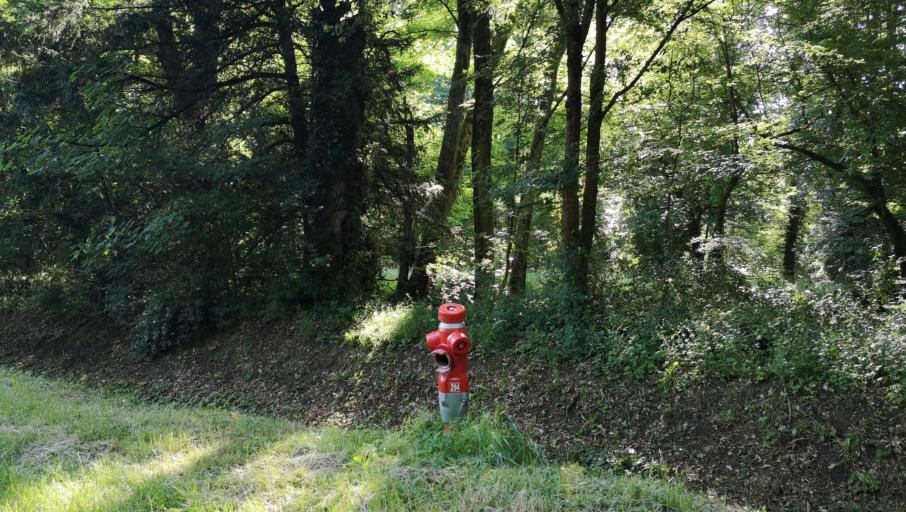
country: FR
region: Centre
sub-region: Departement du Loiret
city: Saint-Jean-de-Braye
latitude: 47.9229
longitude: 1.9815
